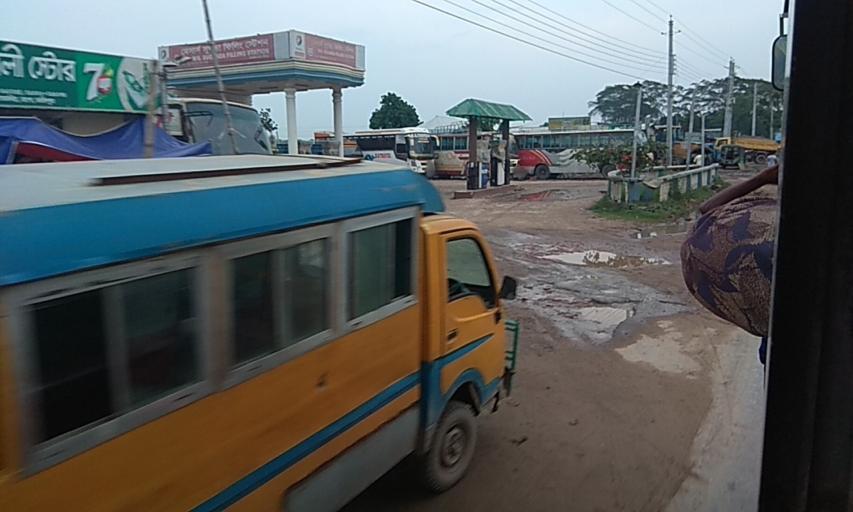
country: BD
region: Dhaka
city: Char Bhadrasan
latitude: 23.3872
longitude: 89.9909
